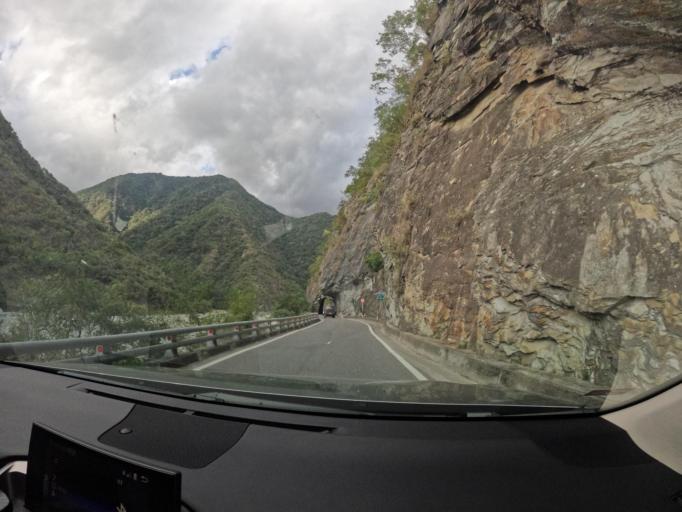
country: TW
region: Taiwan
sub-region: Taitung
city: Taitung
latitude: 23.1345
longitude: 121.1223
